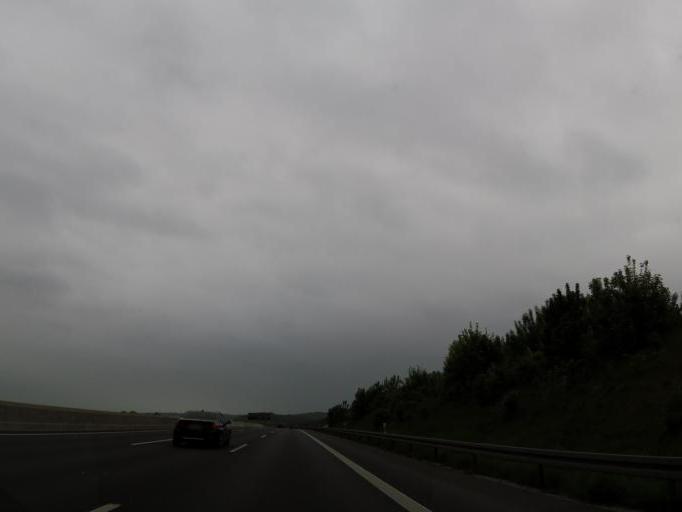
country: DE
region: Lower Saxony
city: Norten-Hardenberg
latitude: 51.6234
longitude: 9.9142
